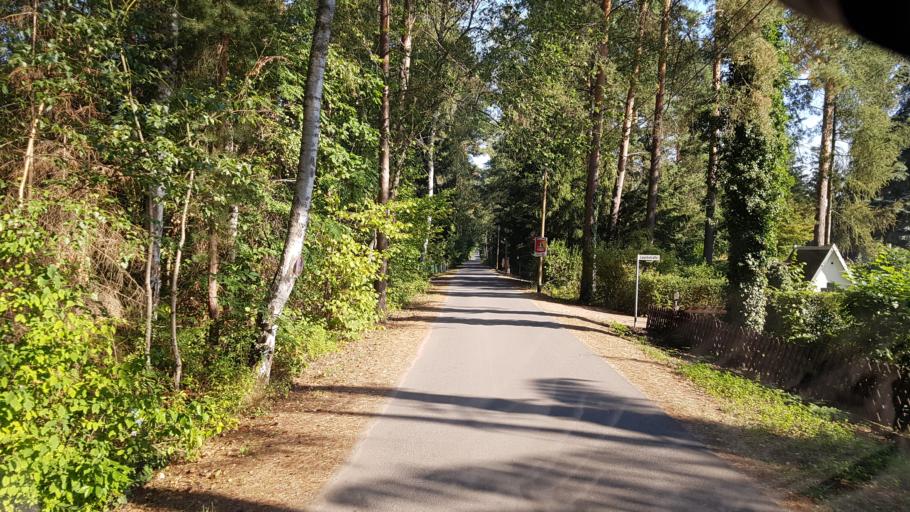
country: DE
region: Brandenburg
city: Plessa
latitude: 51.5141
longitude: 13.6515
